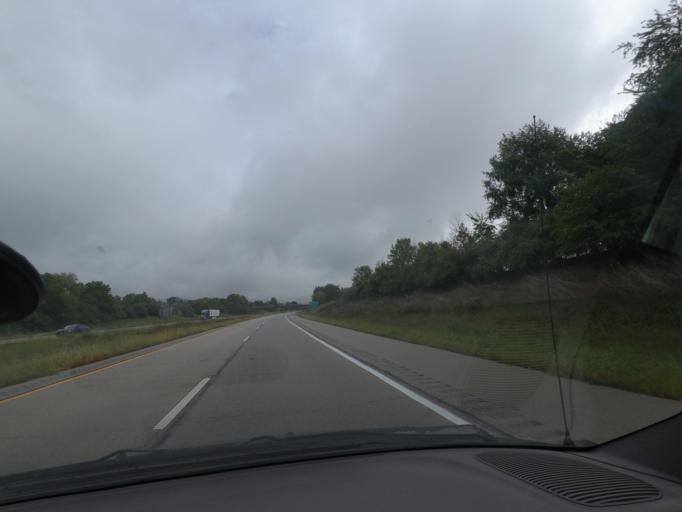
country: US
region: Illinois
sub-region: Piatt County
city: Monticello
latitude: 40.0696
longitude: -88.5444
